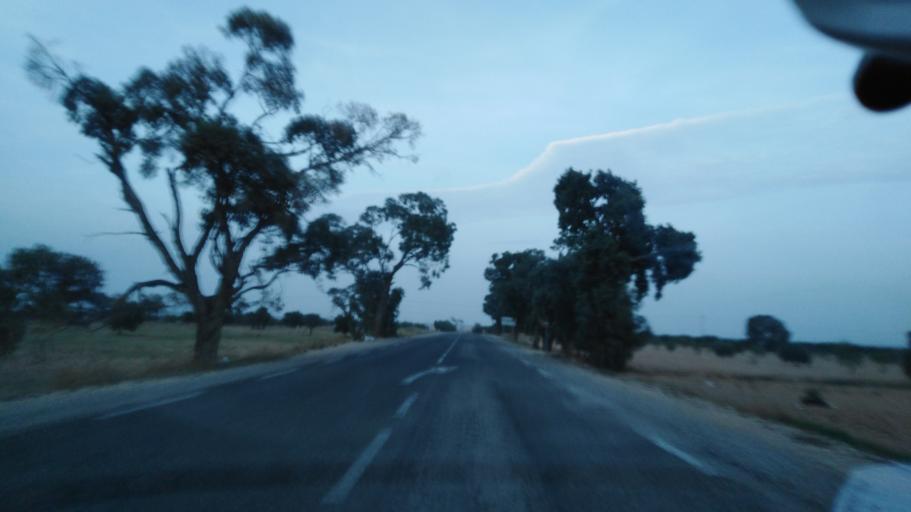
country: TN
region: Al Mahdiyah
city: Shurban
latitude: 34.9449
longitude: 10.4038
